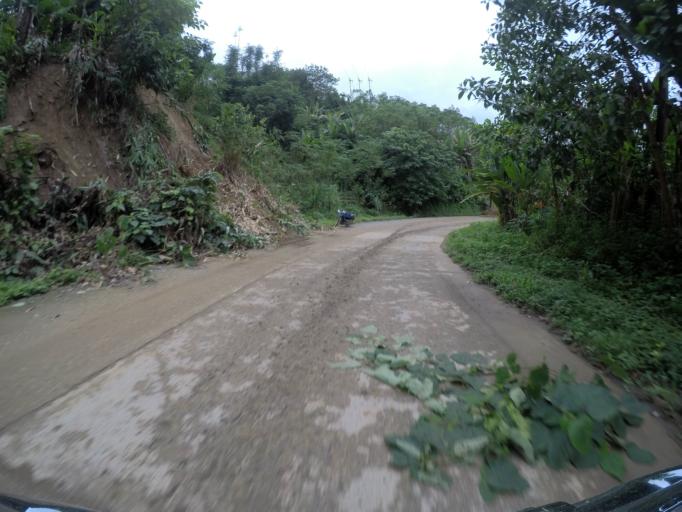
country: VN
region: Quang Nam
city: Prao
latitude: 15.6342
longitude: 107.5480
